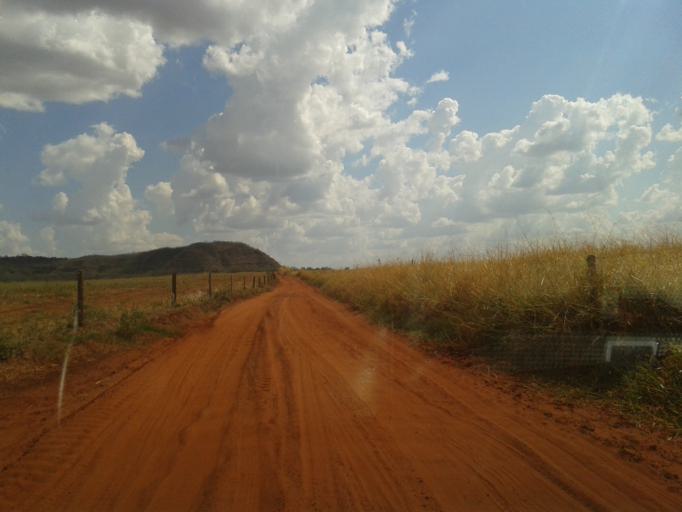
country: BR
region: Minas Gerais
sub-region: Santa Vitoria
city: Santa Vitoria
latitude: -19.1969
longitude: -49.9247
